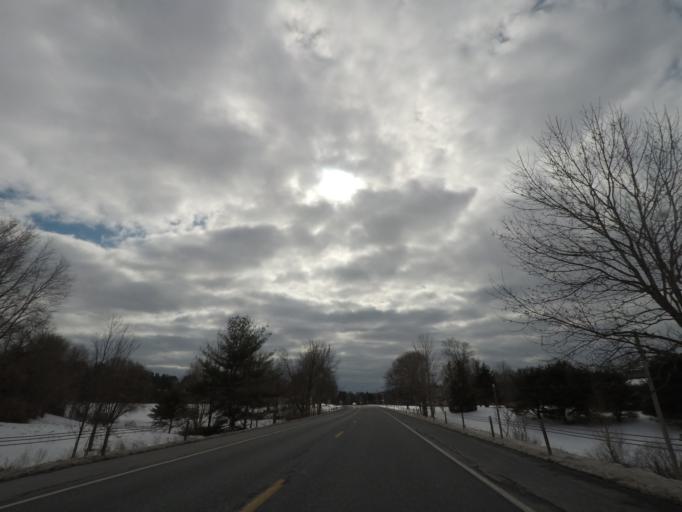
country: US
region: New York
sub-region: Washington County
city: Cambridge
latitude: 42.9735
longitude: -73.3770
